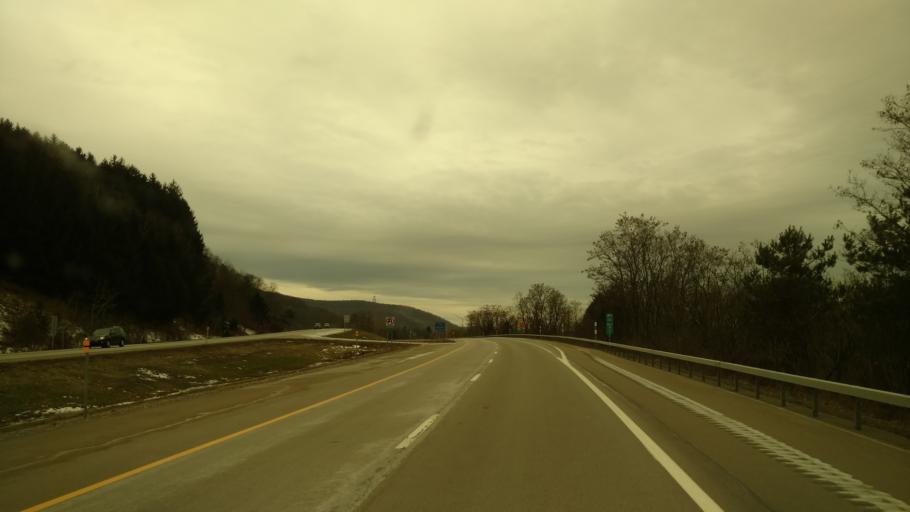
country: US
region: New York
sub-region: Cattaraugus County
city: Salamanca
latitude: 42.1518
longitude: -78.6981
